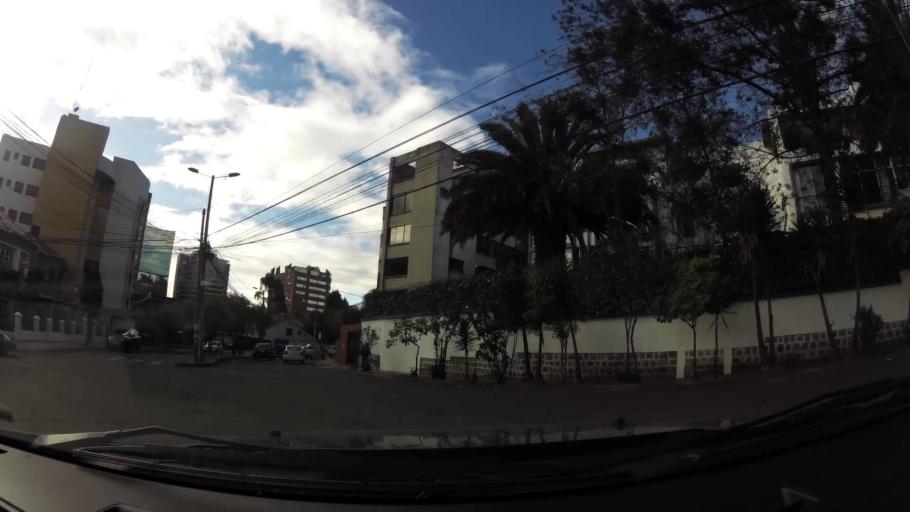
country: EC
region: Pichincha
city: Quito
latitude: -0.2047
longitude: -78.4810
